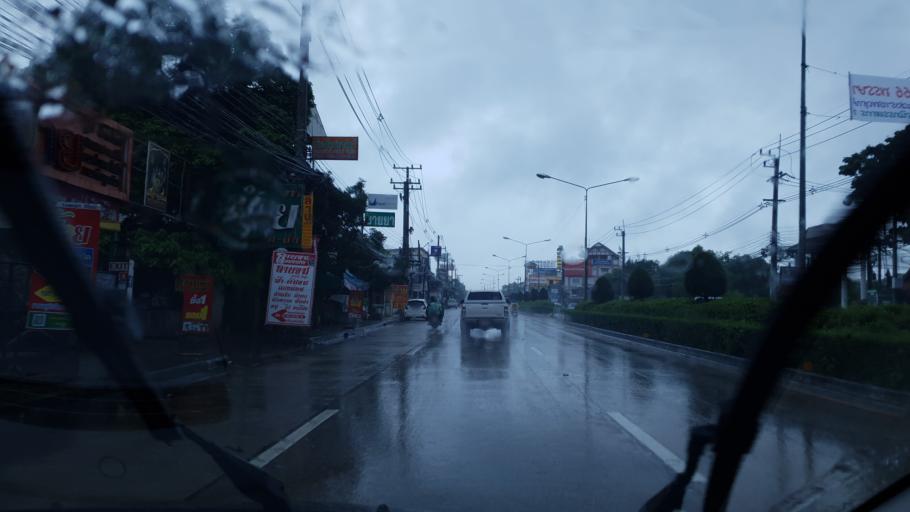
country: TH
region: Chiang Mai
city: Chiang Mai
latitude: 18.7371
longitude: 98.9558
